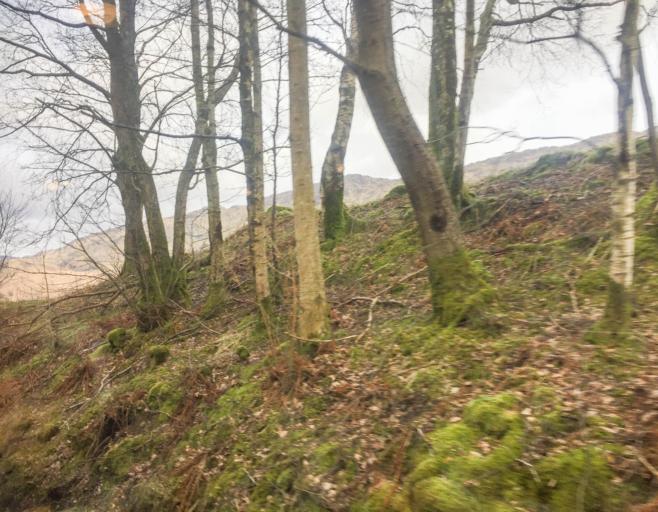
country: GB
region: Scotland
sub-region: Argyll and Bute
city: Garelochhead
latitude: 56.2903
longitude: -4.7133
